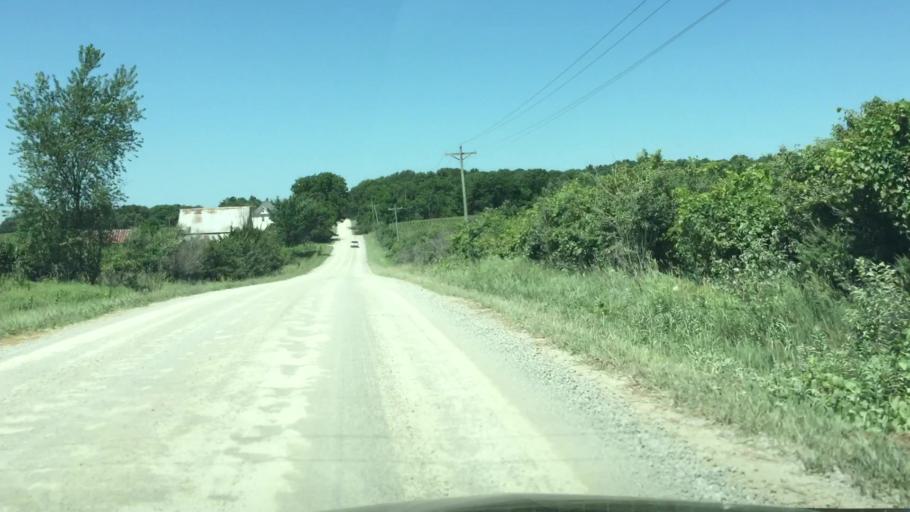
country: US
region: Iowa
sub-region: Linn County
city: Ely
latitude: 41.8329
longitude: -91.5803
